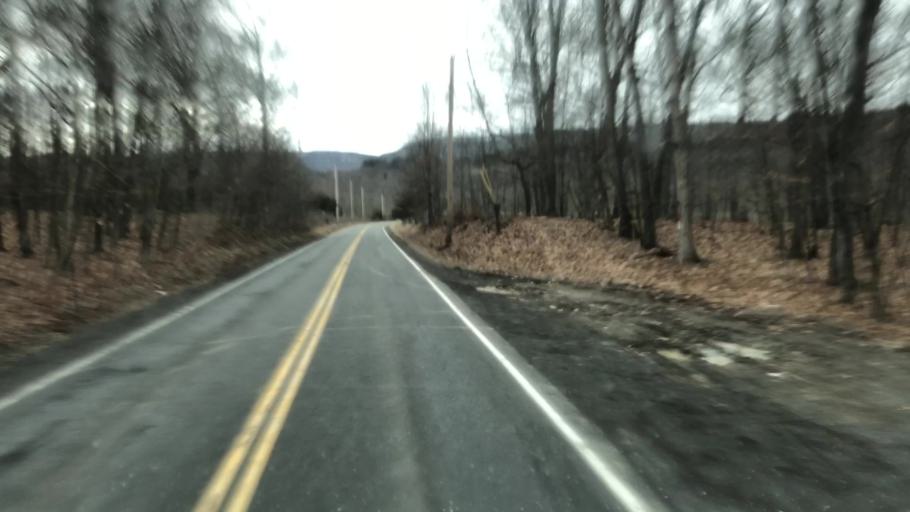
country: US
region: New York
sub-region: Ulster County
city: New Paltz
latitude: 41.7405
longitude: -74.1341
